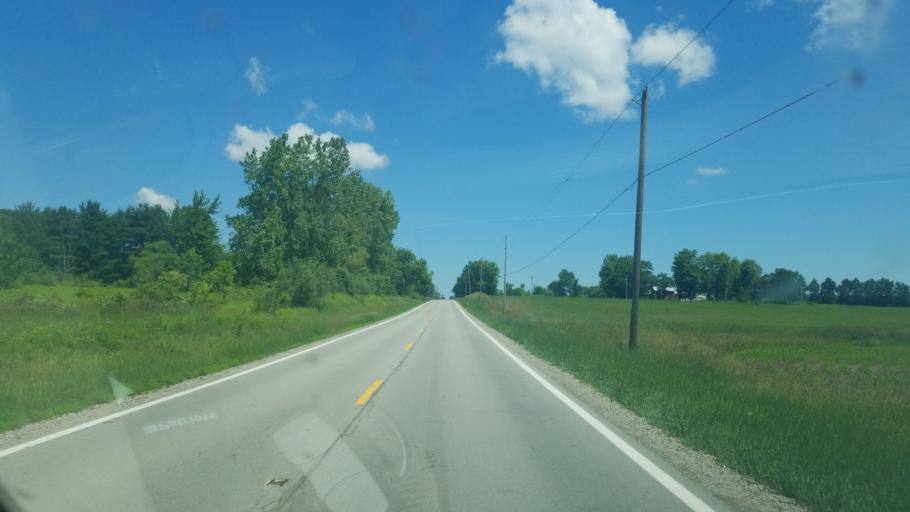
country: US
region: Ohio
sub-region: Huron County
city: New London
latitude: 41.1479
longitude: -82.4099
